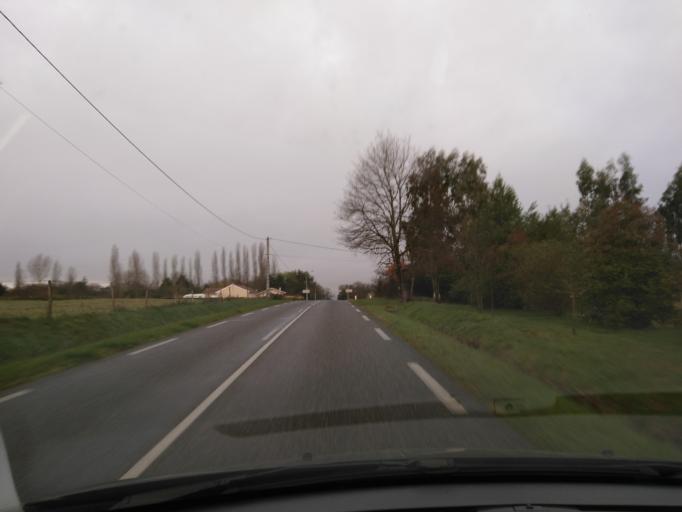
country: FR
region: Midi-Pyrenees
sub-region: Departement de la Haute-Garonne
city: Montesquieu-Volvestre
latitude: 43.1611
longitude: 1.2785
